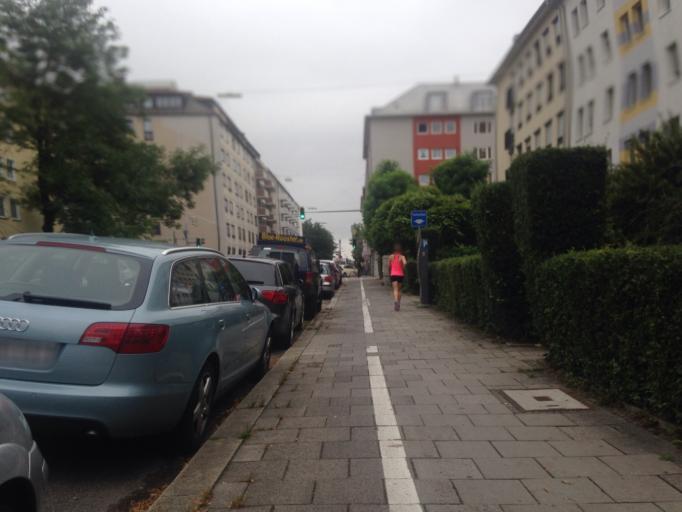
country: DE
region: Bavaria
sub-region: Upper Bavaria
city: Munich
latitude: 48.1523
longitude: 11.5710
